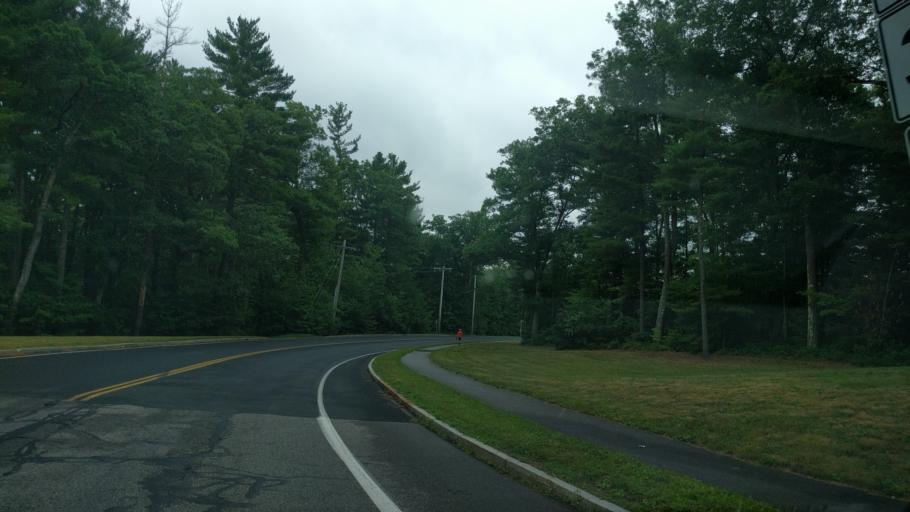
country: US
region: Massachusetts
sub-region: Worcester County
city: Grafton
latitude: 42.2506
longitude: -71.6845
